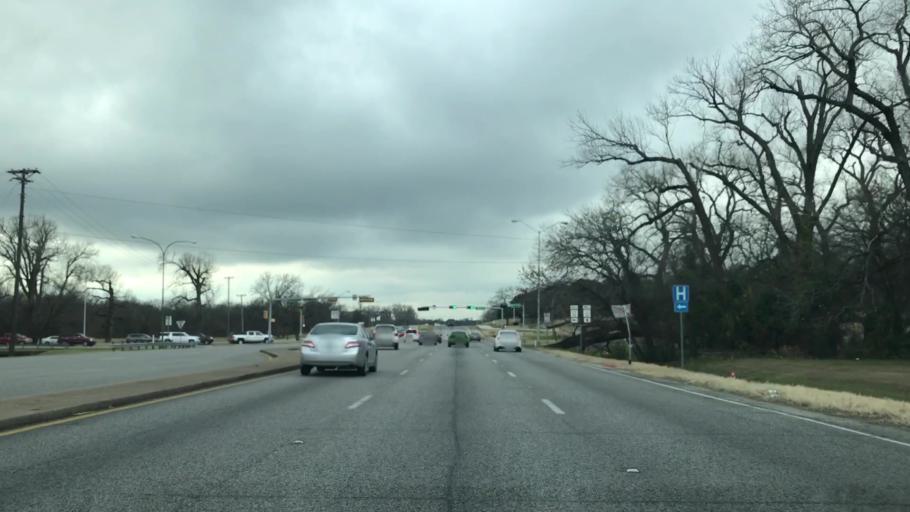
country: US
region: Texas
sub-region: Dallas County
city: Highland Park
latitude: 32.8616
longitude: -96.7185
